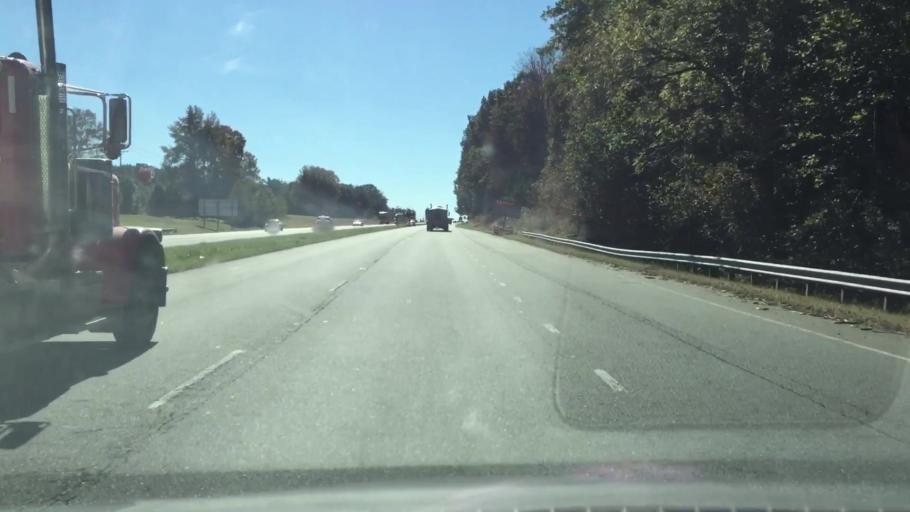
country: US
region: North Carolina
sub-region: Guilford County
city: McLeansville
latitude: 36.1719
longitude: -79.7144
